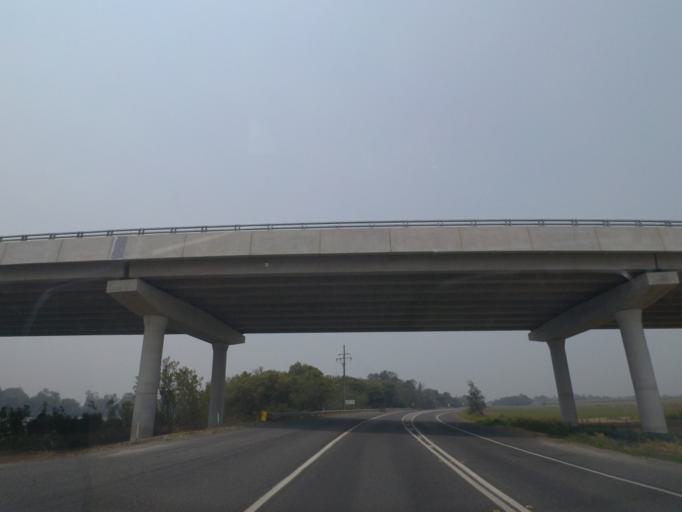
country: AU
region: New South Wales
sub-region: Richmond Valley
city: Evans Head
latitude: -28.9996
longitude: 153.4406
